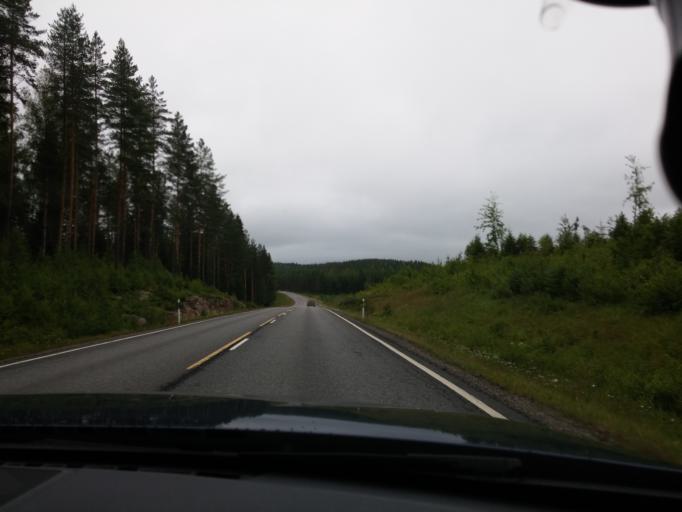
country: FI
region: Pirkanmaa
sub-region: Ylae-Pirkanmaa
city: Maenttae
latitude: 61.9566
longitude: 24.5721
